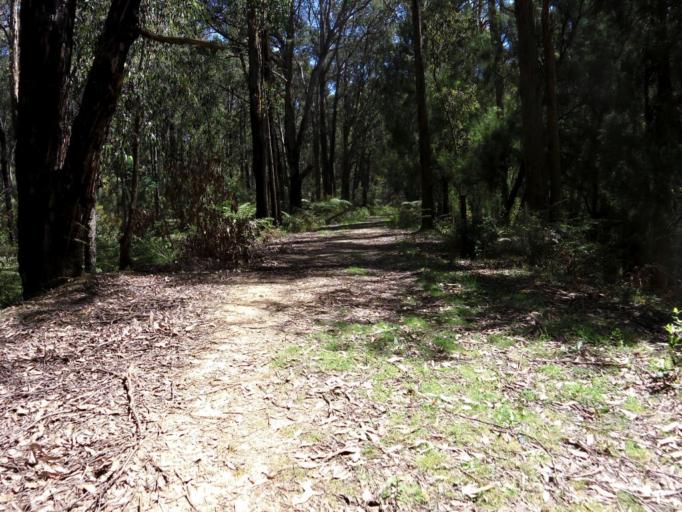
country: AU
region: Victoria
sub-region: Baw Baw
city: Warragul
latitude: -37.9035
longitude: 145.9788
